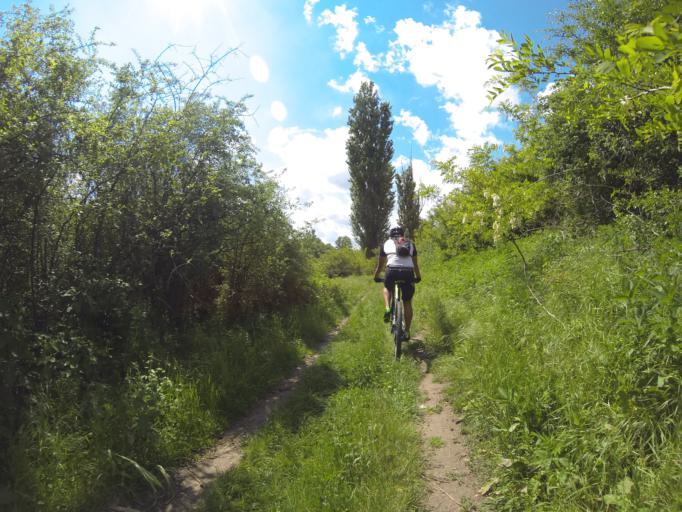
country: RO
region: Dolj
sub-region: Comuna Malu Mare
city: Preajba
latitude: 44.2654
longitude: 23.8575
